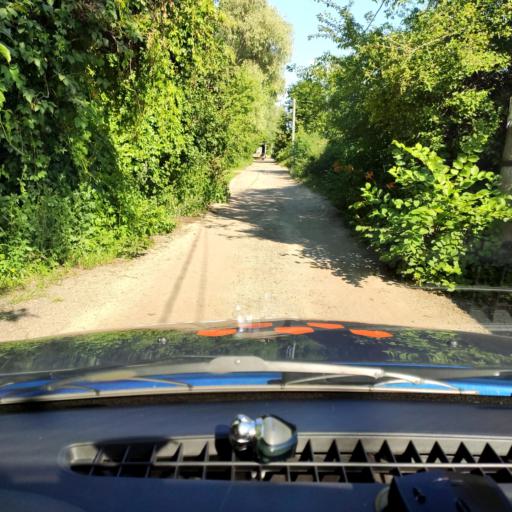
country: RU
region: Voronezj
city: Strelitsa
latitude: 51.6107
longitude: 38.8916
